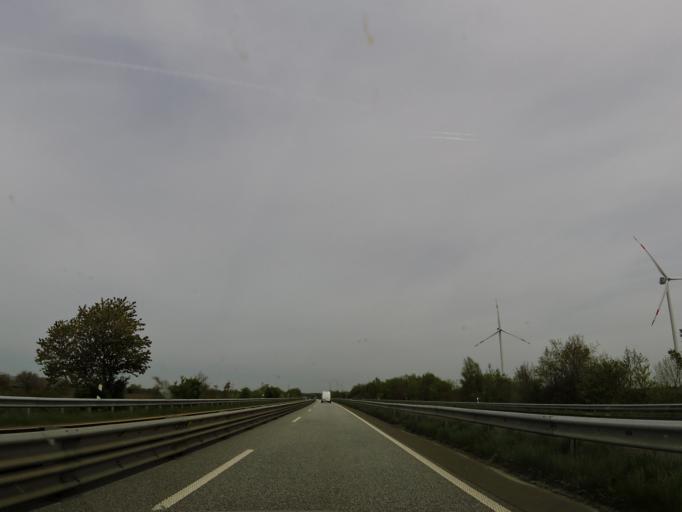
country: DE
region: Schleswig-Holstein
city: Tensbuttel-Rost
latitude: 54.1022
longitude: 9.2651
